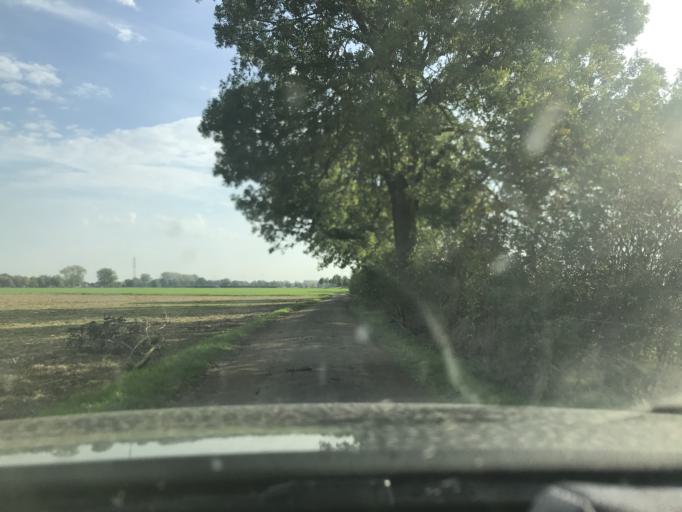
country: DE
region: North Rhine-Westphalia
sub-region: Regierungsbezirk Dusseldorf
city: Kleve
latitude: 51.8178
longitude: 6.1897
